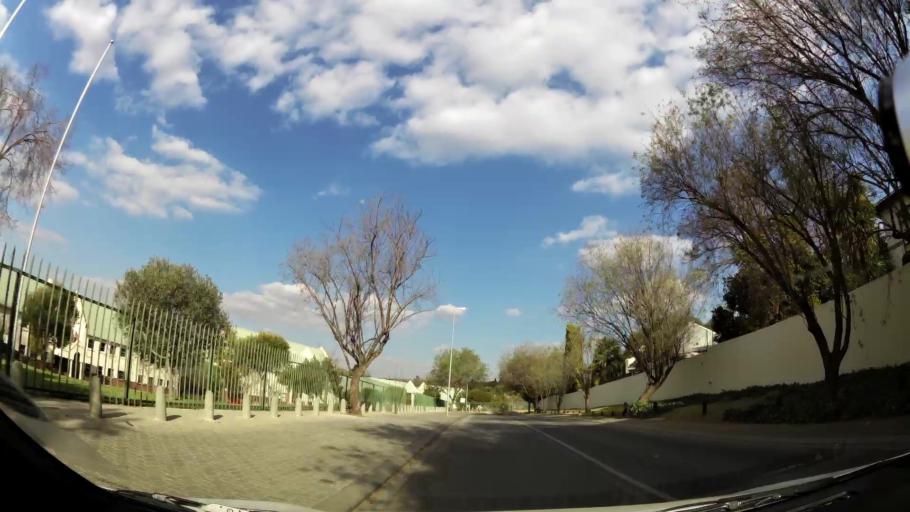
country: ZA
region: Gauteng
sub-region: City of Johannesburg Metropolitan Municipality
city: Diepsloot
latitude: -26.0083
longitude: 28.0326
